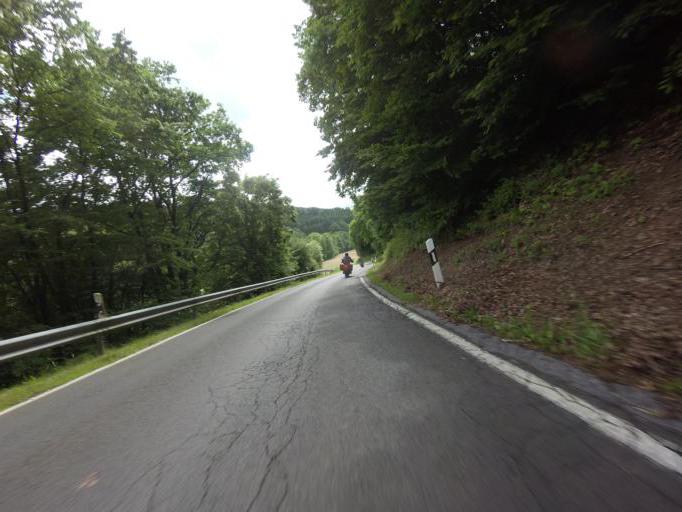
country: DE
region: Rheinland-Pfalz
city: Reudelsterz
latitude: 50.2956
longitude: 7.1388
